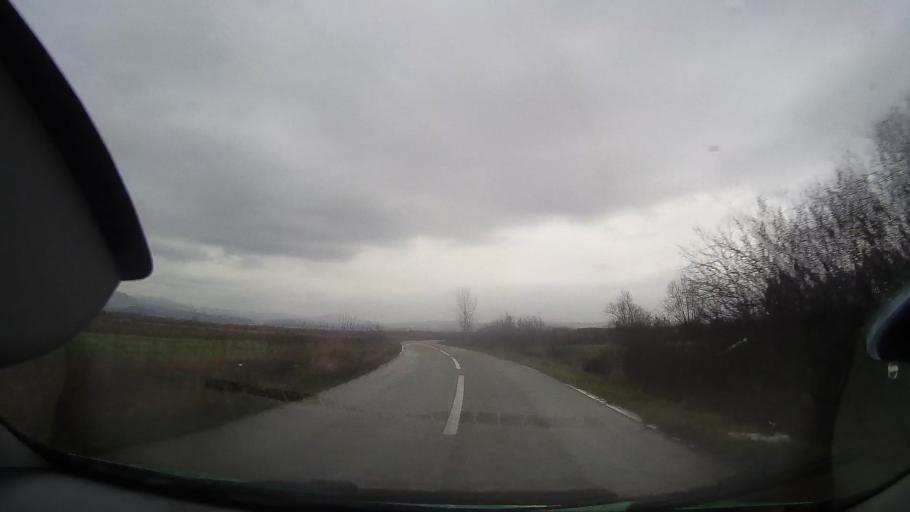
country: RO
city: Capalna
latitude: 46.7289
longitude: 22.0922
